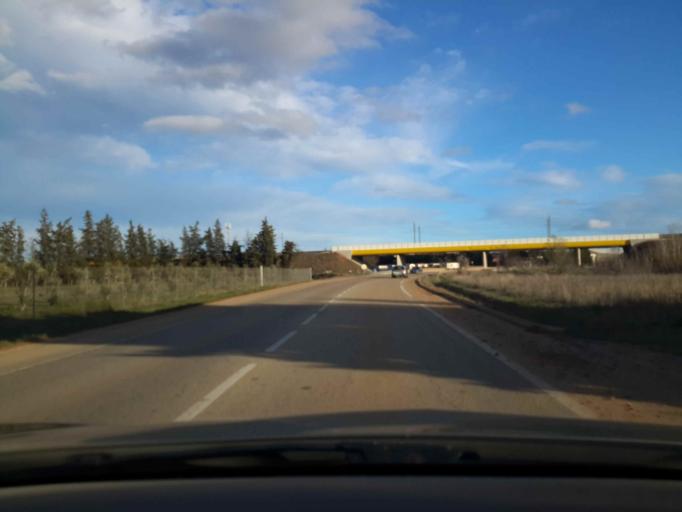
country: FR
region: Languedoc-Roussillon
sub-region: Departement du Gard
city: Aubord
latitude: 43.7582
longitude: 4.3392
